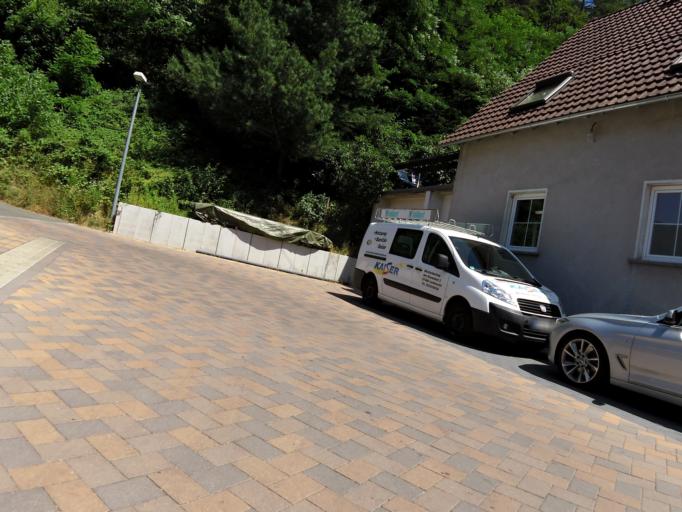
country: DE
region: Rheinland-Pfalz
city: Frankeneck
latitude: 49.3570
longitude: 8.0270
